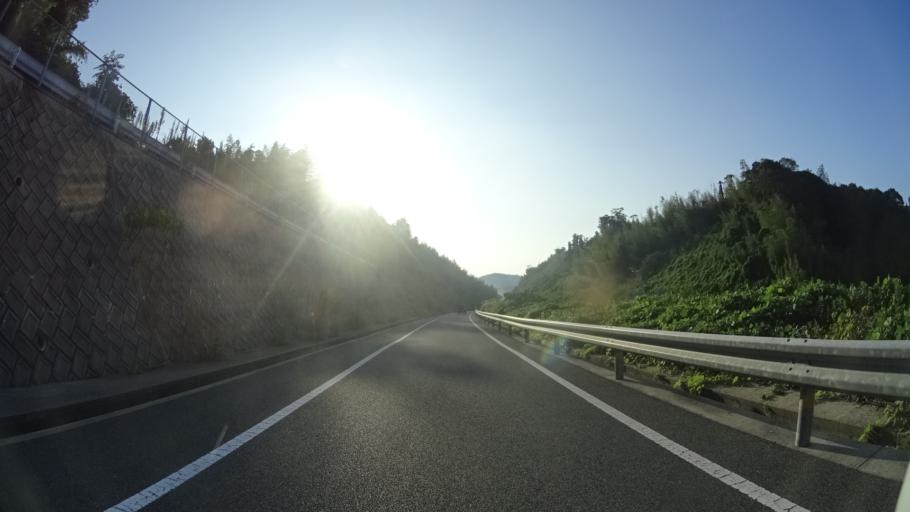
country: JP
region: Yamaguchi
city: Hagi
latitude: 34.3855
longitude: 131.3488
